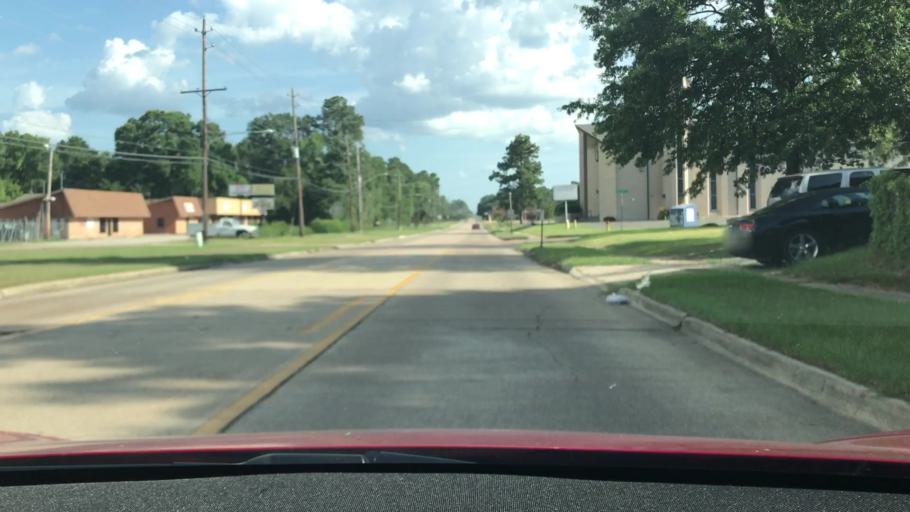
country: US
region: Louisiana
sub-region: Bossier Parish
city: Bossier City
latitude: 32.4117
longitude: -93.7804
